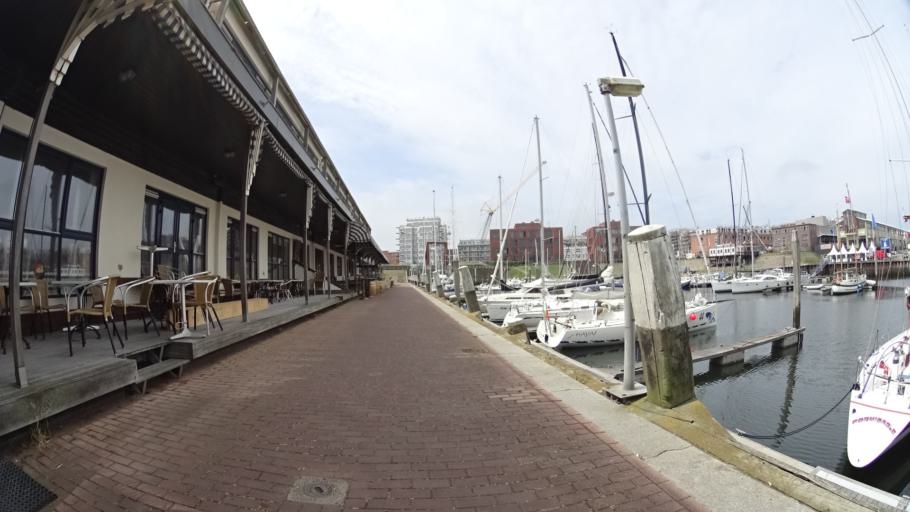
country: NL
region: South Holland
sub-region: Gemeente Den Haag
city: Scheveningen
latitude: 52.0951
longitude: 4.2654
